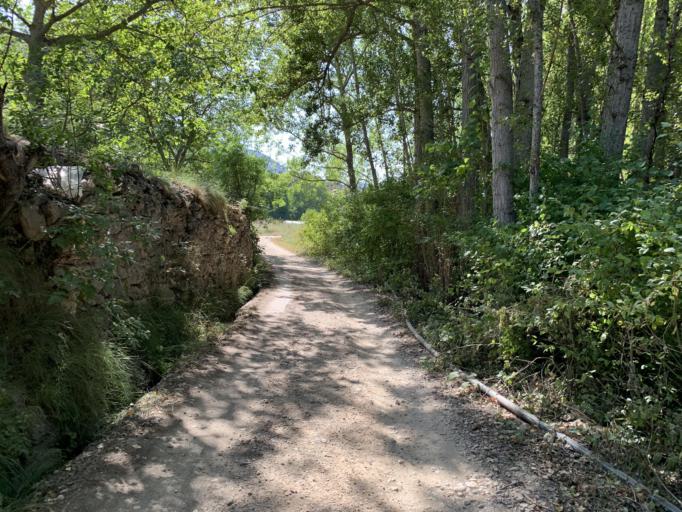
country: ES
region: Castille-La Mancha
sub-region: Provincia de Guadalajara
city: Ocentejo
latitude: 40.7683
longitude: -2.3969
